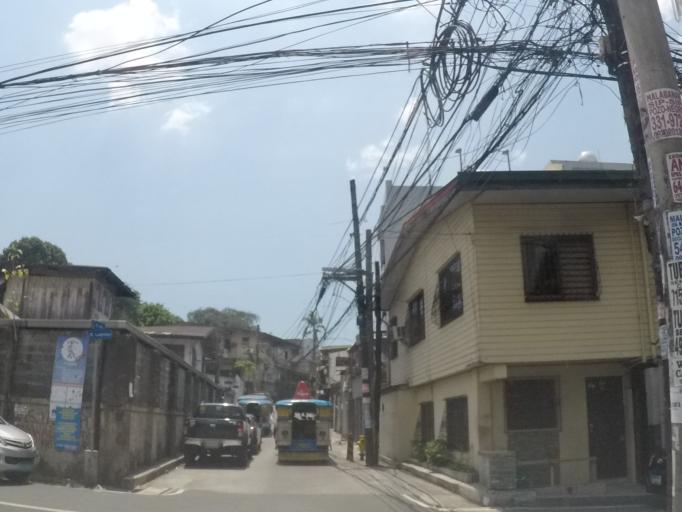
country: PH
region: Metro Manila
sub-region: San Juan
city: San Juan
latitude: 14.6078
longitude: 121.0246
